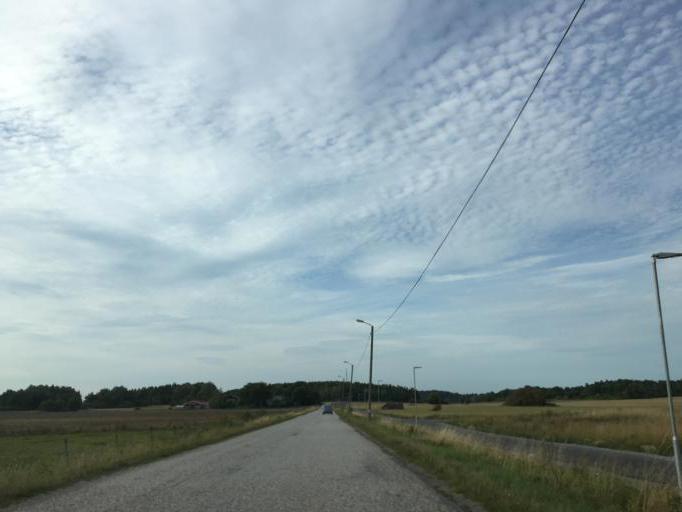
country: SE
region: Soedermanland
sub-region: Eskilstuna Kommun
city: Torshalla
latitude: 59.4400
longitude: 16.4739
